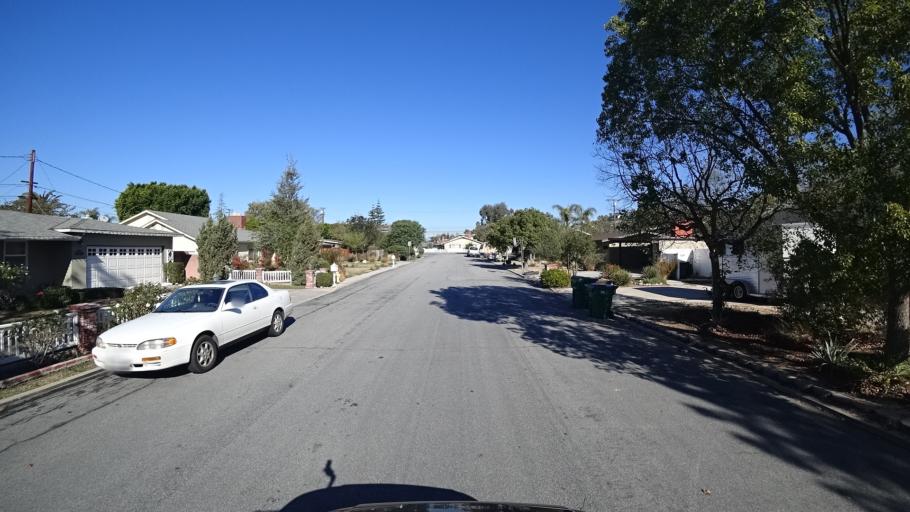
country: US
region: California
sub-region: Orange County
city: North Tustin
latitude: 33.7726
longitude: -117.8067
